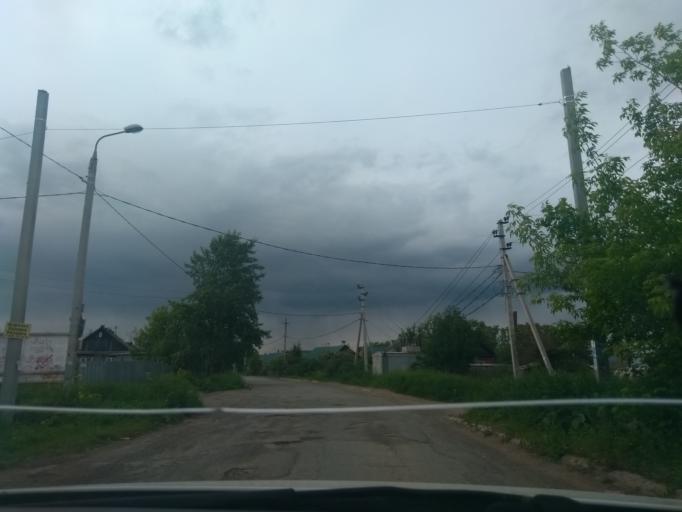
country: RU
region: Perm
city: Perm
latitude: 57.9957
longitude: 56.3374
